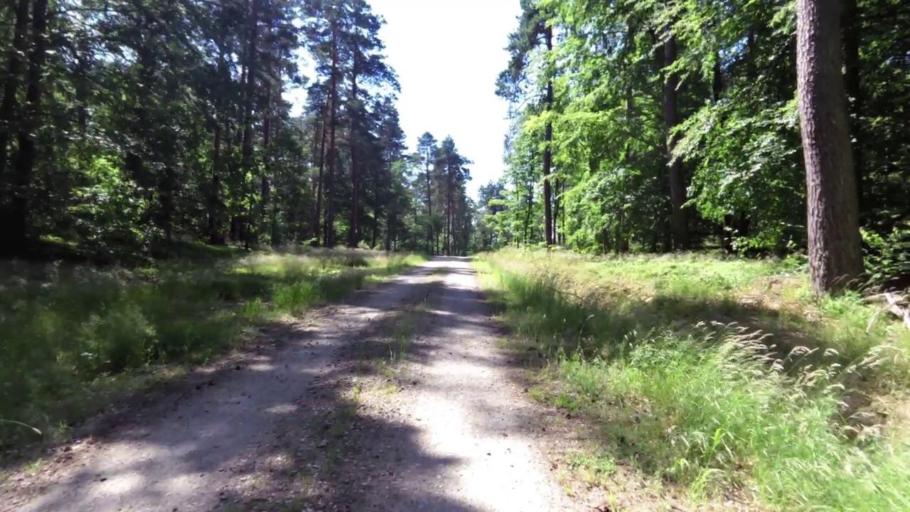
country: PL
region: West Pomeranian Voivodeship
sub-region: Powiat swidwinski
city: Polczyn-Zdroj
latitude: 53.8062
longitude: 16.1221
